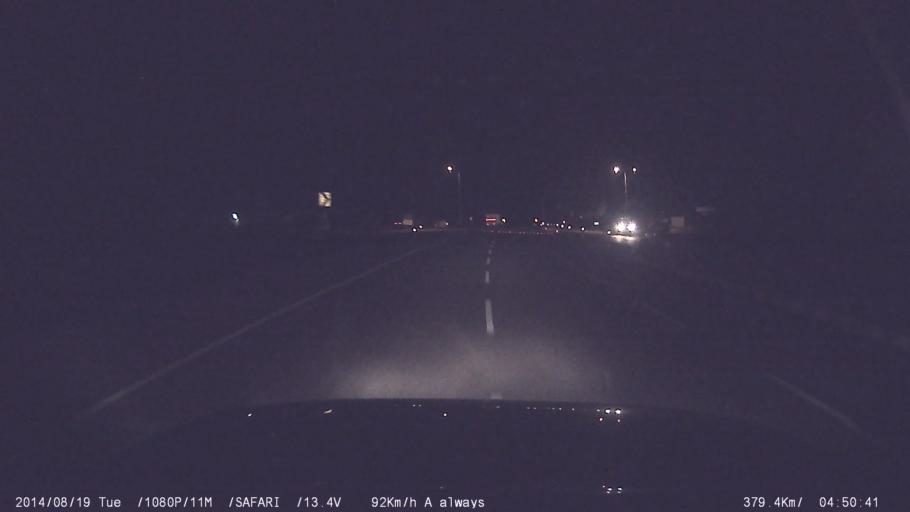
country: IN
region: Tamil Nadu
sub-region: Erode
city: Bhavani
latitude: 11.4522
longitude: 77.7794
